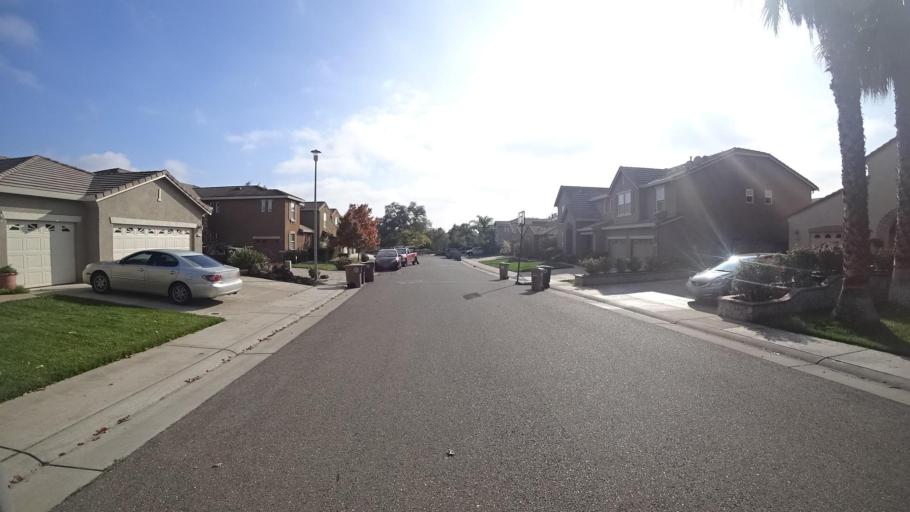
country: US
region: California
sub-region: Sacramento County
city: Vineyard
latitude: 38.4516
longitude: -121.3477
